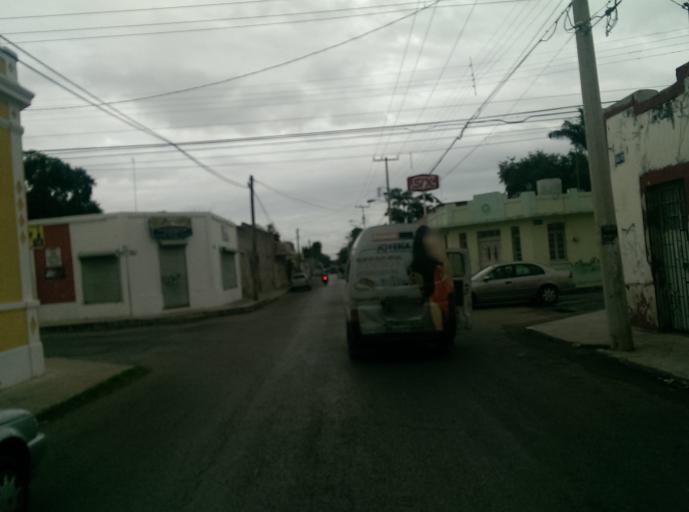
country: MX
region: Yucatan
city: Merida
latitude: 20.9784
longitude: -89.6373
